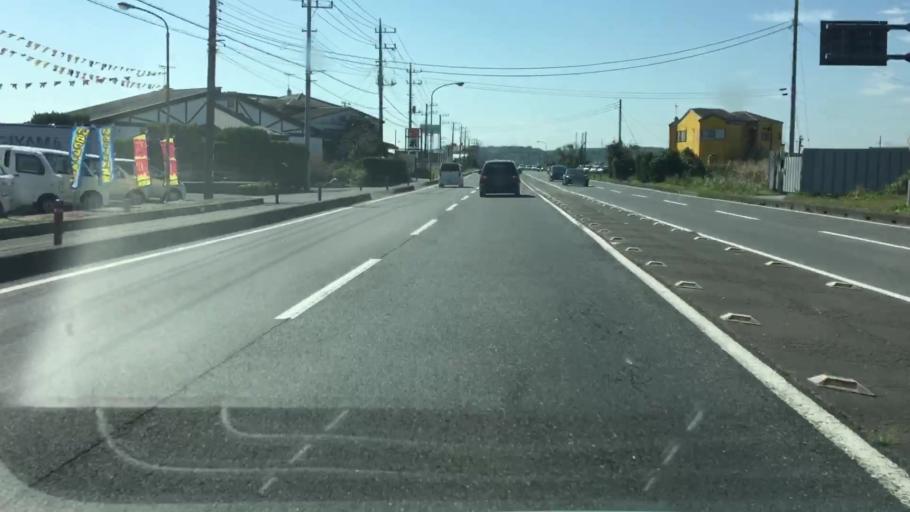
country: JP
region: Ibaraki
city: Ryugasaki
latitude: 35.8954
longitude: 140.1641
